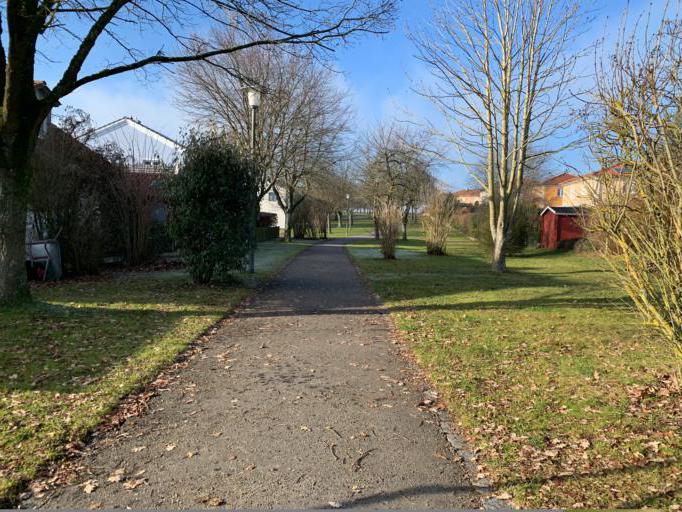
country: DE
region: Bavaria
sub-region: Upper Bavaria
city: Stammham
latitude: 48.8595
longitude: 11.4505
